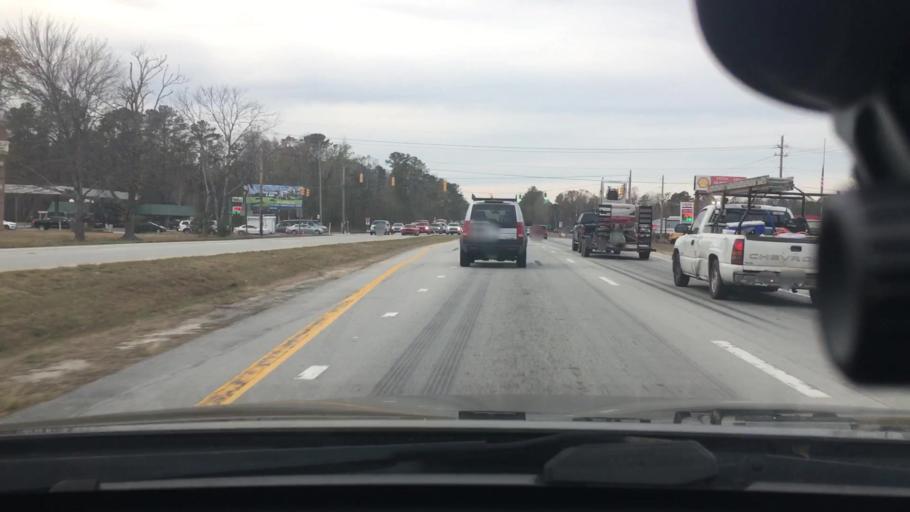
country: US
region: North Carolina
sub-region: Craven County
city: Fairfield Harbour
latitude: 35.0370
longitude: -77.0066
